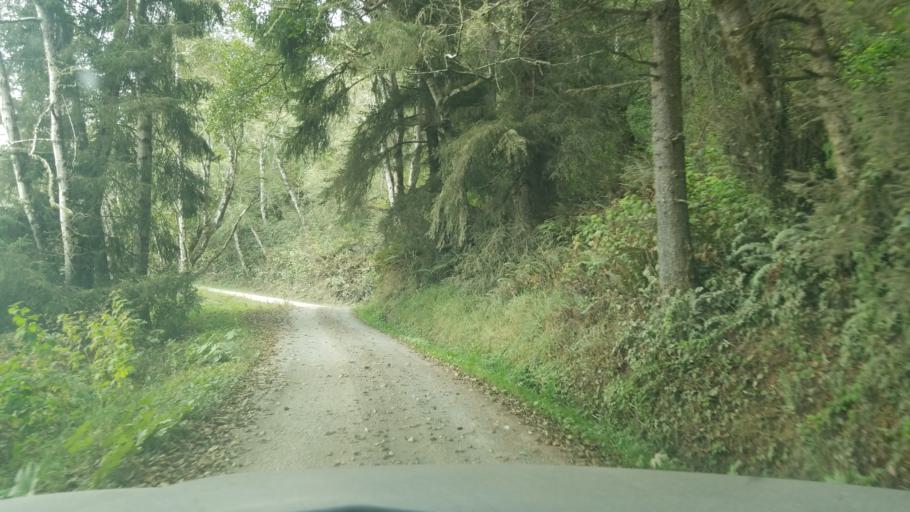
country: US
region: California
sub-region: Del Norte County
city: Bertsch-Oceanview
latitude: 41.5221
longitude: -124.0781
